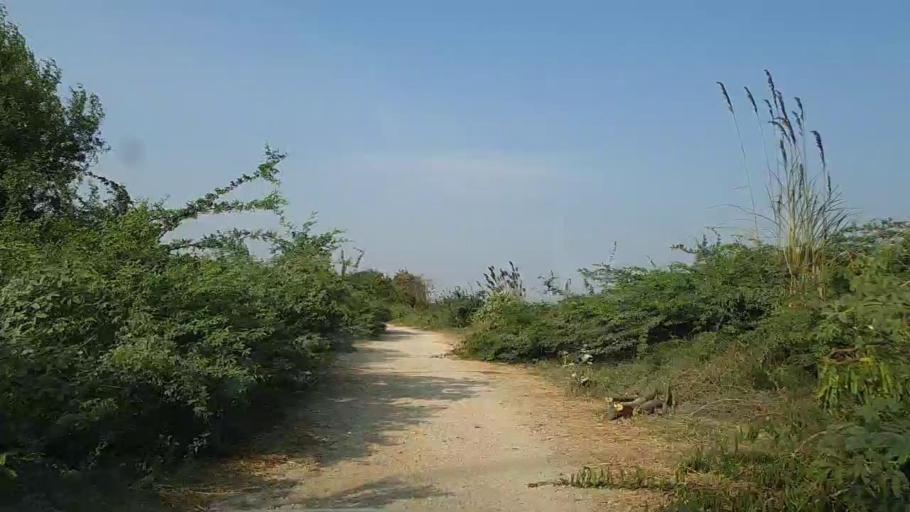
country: PK
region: Sindh
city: Mirpur Sakro
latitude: 24.5971
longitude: 67.6489
